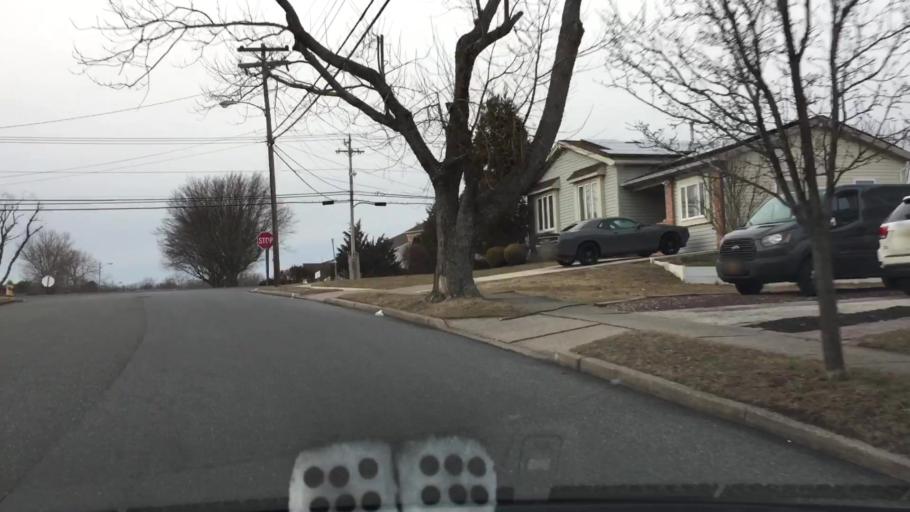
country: US
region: New Jersey
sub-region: Gloucester County
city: Turnersville
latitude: 39.7697
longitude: -75.0592
